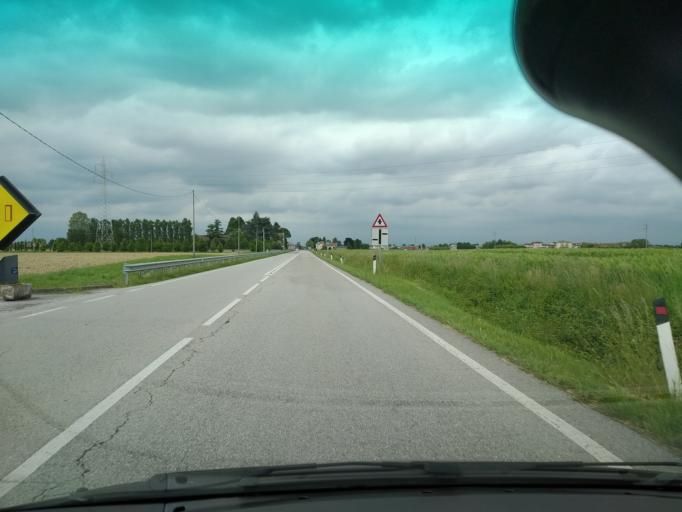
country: IT
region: Veneto
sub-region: Provincia di Padova
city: Tremignon
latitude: 45.5123
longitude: 11.8110
